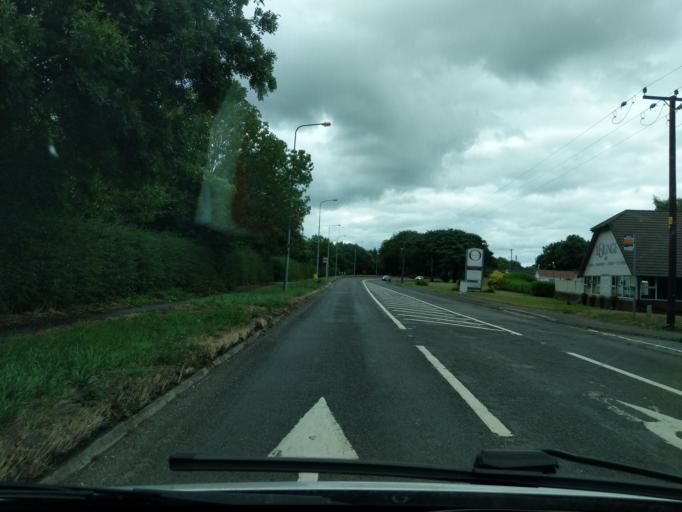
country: GB
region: England
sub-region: Cheshire West and Chester
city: Oakmere
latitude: 53.2251
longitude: -2.6305
